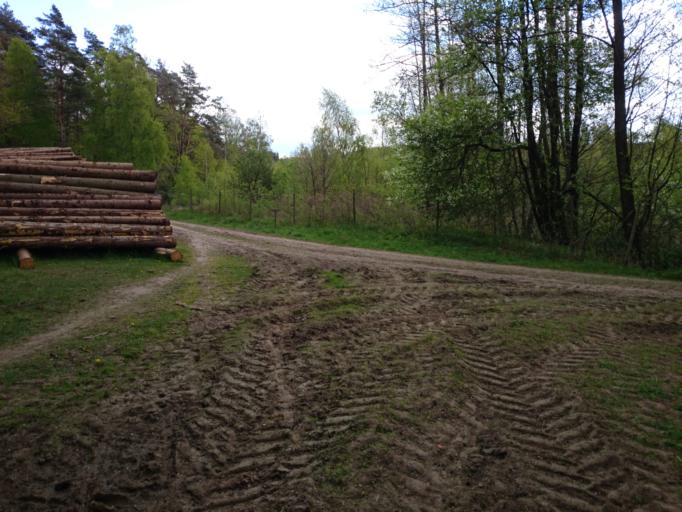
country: SE
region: Skane
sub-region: Lunds Kommun
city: Veberod
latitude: 55.5951
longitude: 13.4423
